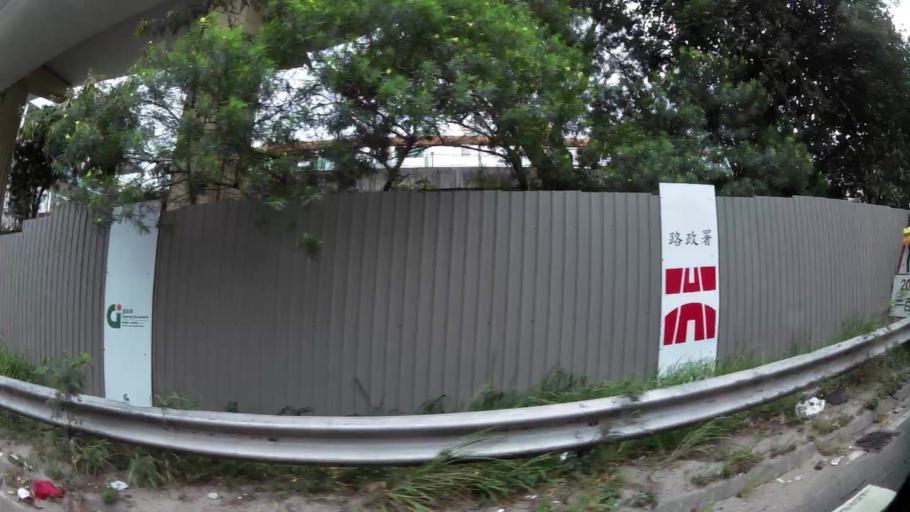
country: HK
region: Tuen Mun
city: Tuen Mun
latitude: 22.4065
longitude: 113.9785
